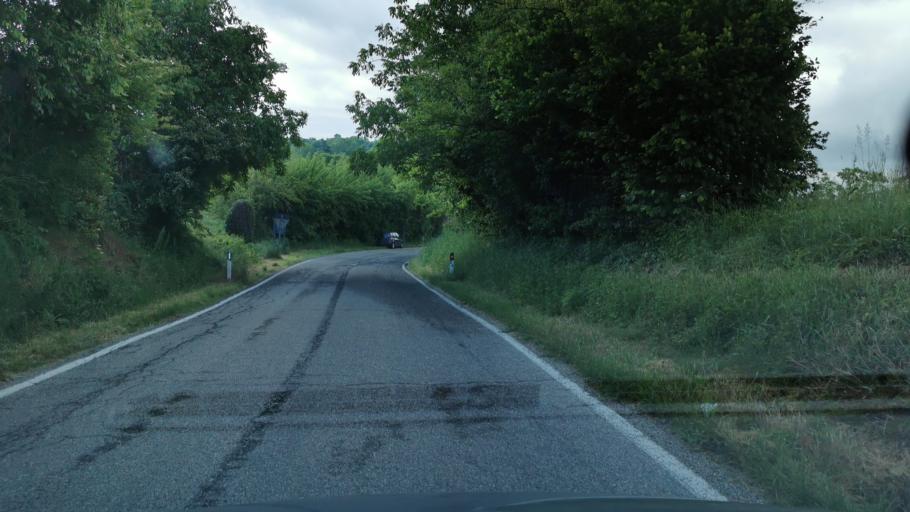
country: IT
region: Piedmont
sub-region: Provincia di Torino
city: Pino Torinese
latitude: 45.0131
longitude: 7.7792
